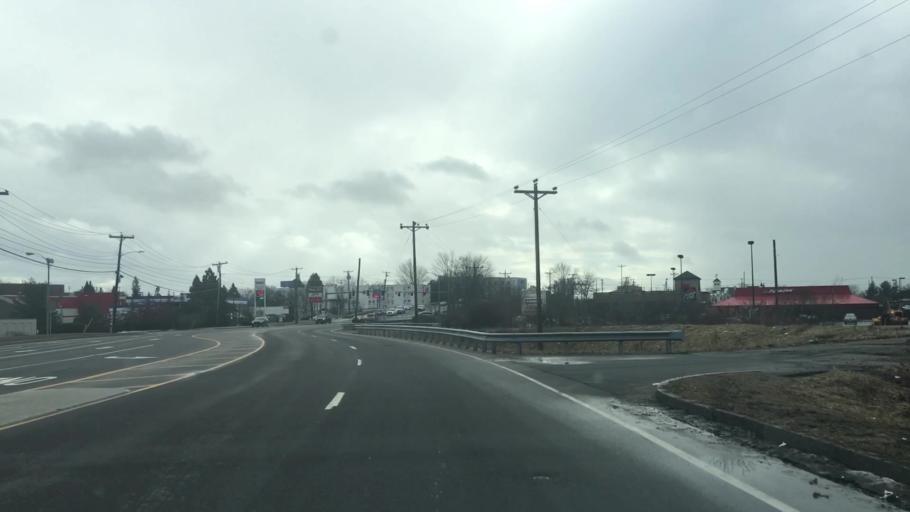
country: US
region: Maine
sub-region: Cumberland County
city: Westbrook
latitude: 43.6805
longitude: -70.3291
